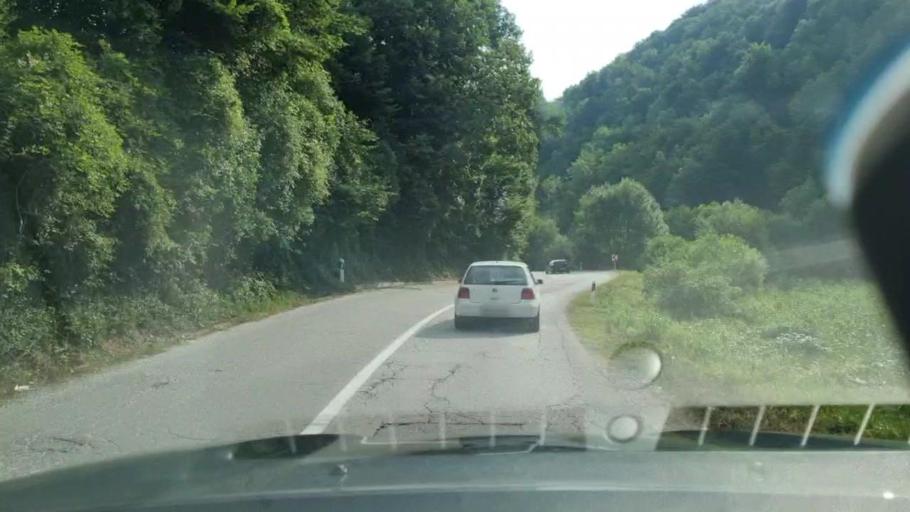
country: BA
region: Federation of Bosnia and Herzegovina
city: Jezerski
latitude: 45.0062
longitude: 16.1130
